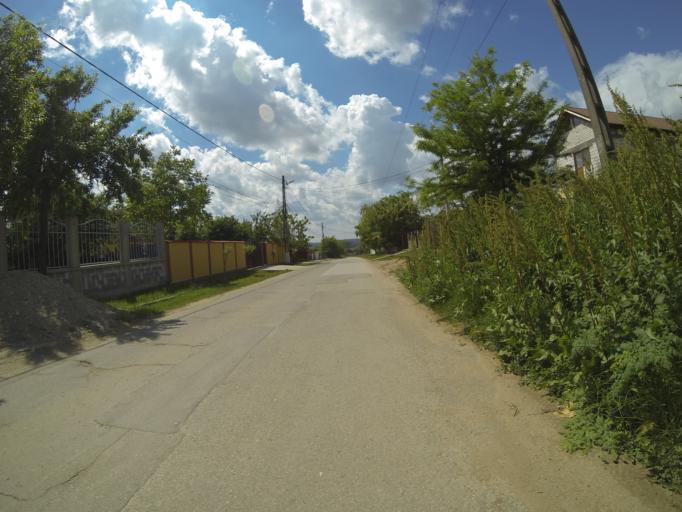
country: RO
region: Dolj
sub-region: Comuna Malu Mare
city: Preajba
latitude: 44.2679
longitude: 23.8373
